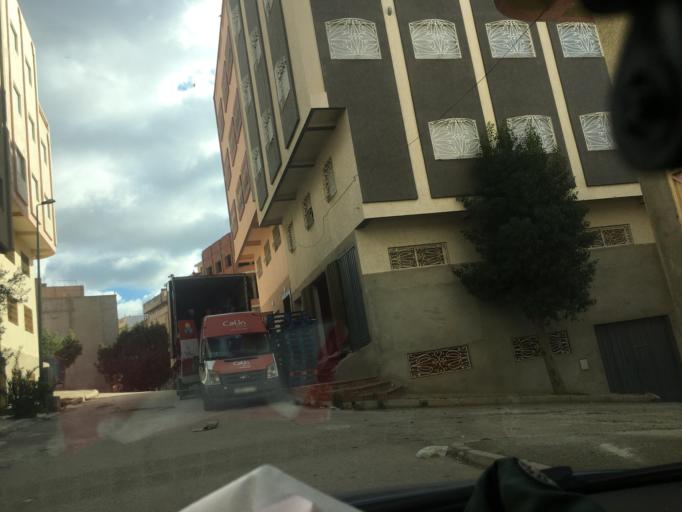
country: MA
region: Tanger-Tetouan
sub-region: Tanger-Assilah
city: Tangier
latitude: 35.7253
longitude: -5.8149
